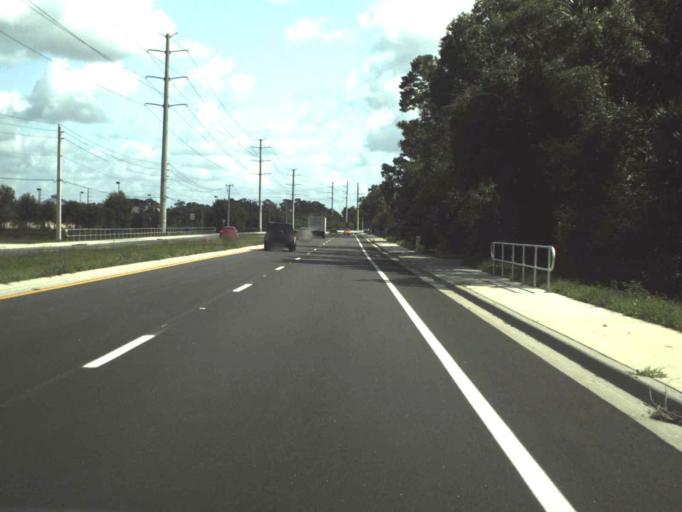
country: US
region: Florida
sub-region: Seminole County
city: Midway
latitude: 28.8664
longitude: -81.1622
